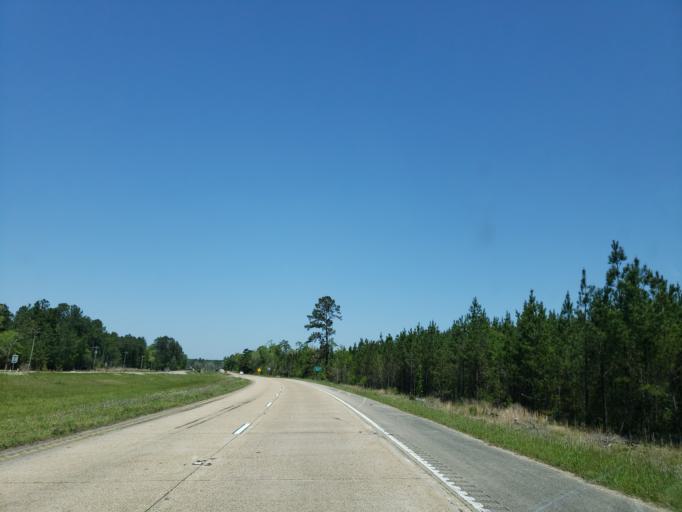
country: US
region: Mississippi
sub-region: Stone County
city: Wiggins
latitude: 31.0469
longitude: -89.2024
